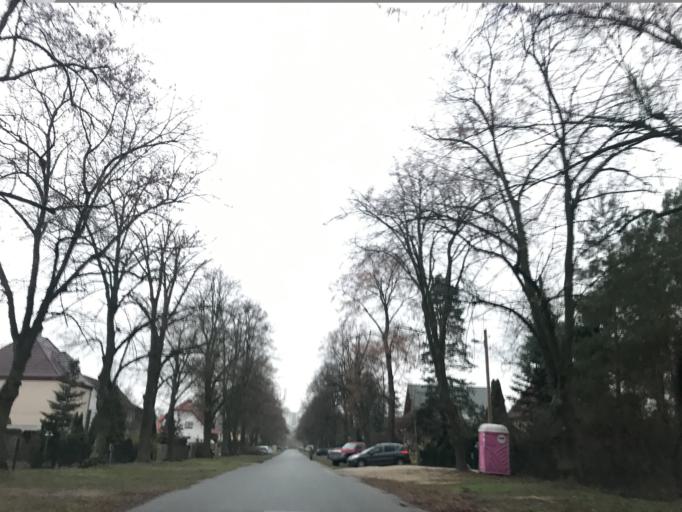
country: DE
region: Brandenburg
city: Falkensee
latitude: 52.5569
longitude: 13.1192
